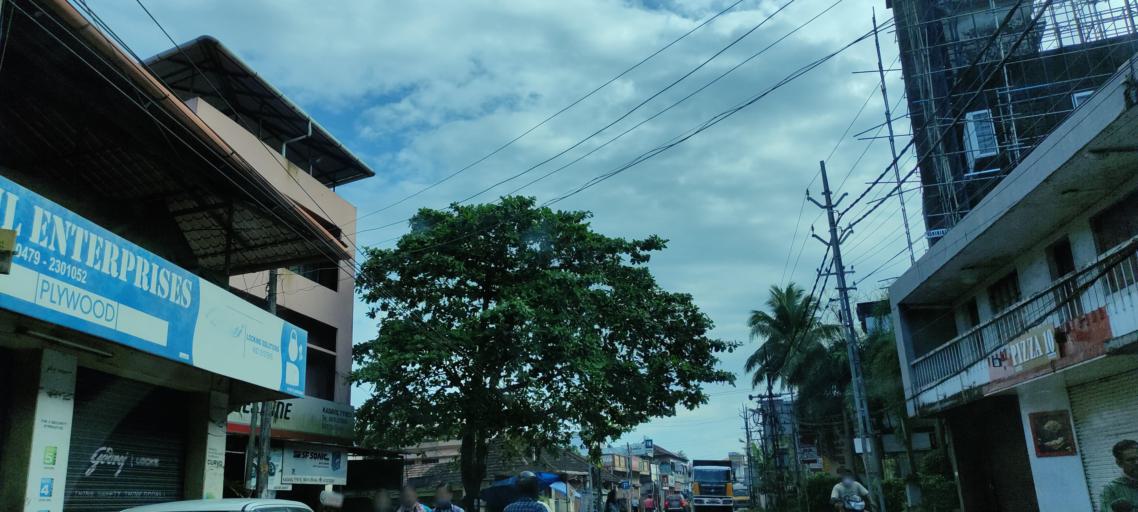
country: IN
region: Kerala
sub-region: Alappuzha
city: Mavelikara
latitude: 9.2522
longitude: 76.5422
